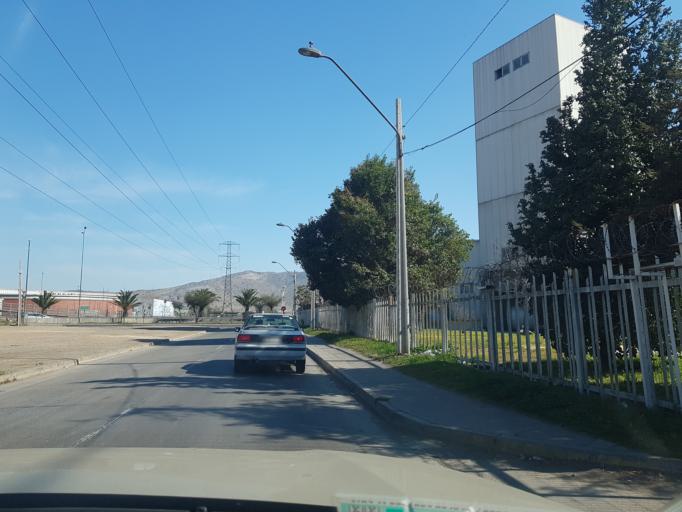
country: CL
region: Santiago Metropolitan
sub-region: Provincia de Santiago
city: Lo Prado
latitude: -33.3724
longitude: -70.7227
